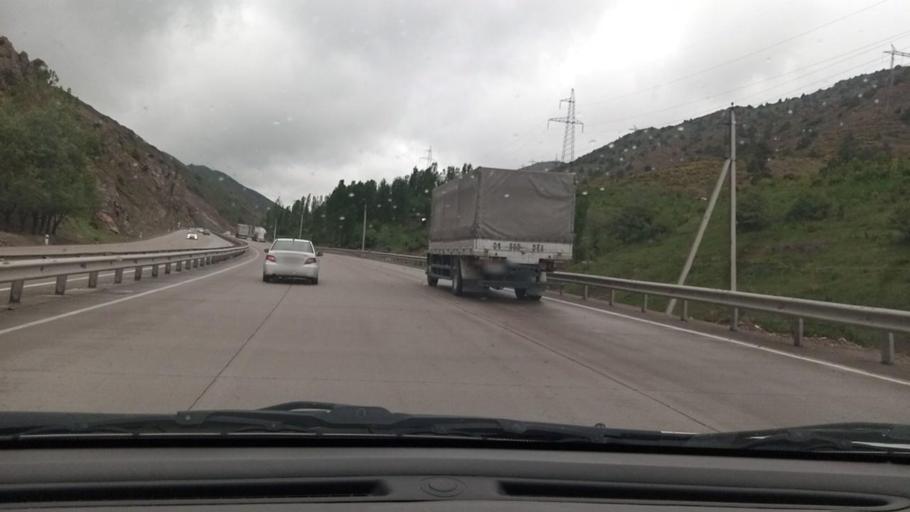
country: UZ
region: Toshkent
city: Angren
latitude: 41.0444
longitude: 70.5742
